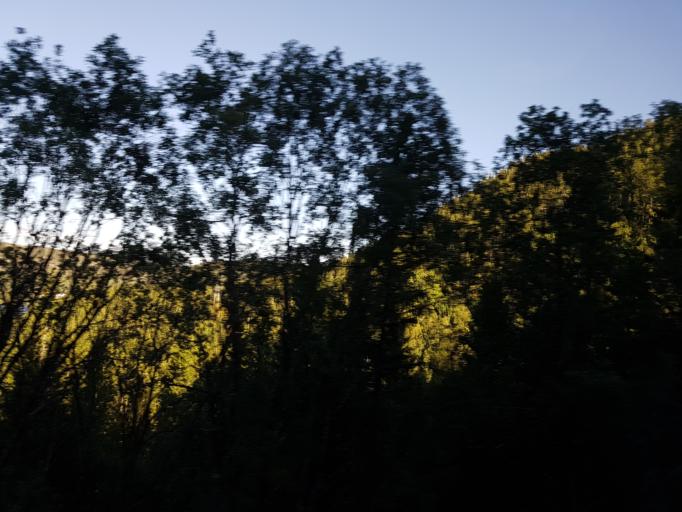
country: NO
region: Sor-Trondelag
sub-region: Afjord
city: A i Afjord
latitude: 63.7762
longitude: 10.2344
